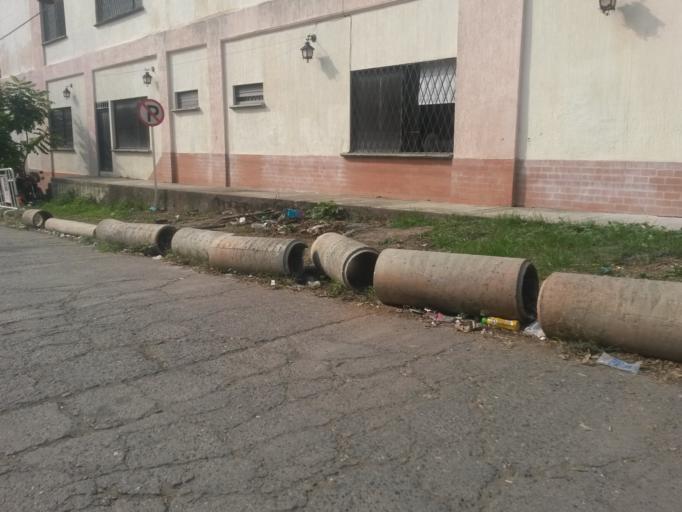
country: CO
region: Cauca
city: El Bordo
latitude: 2.1132
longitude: -76.9859
